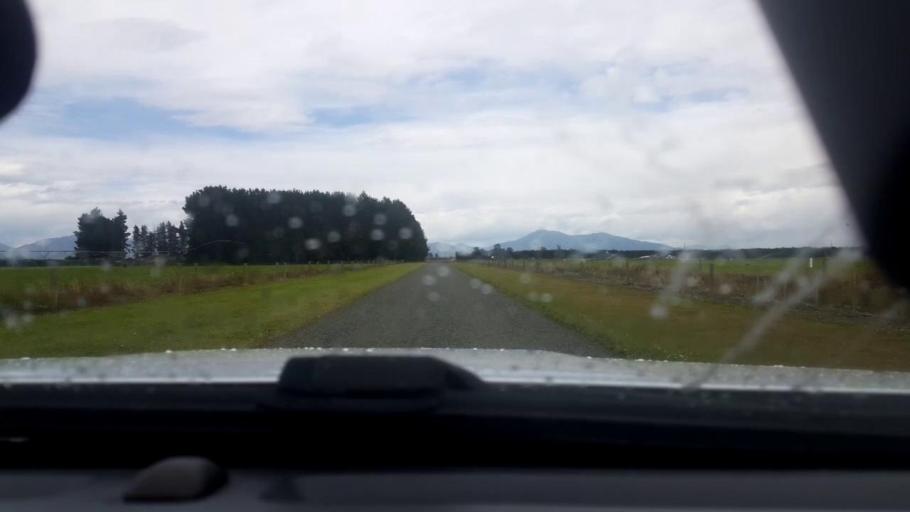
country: NZ
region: Canterbury
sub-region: Timaru District
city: Pleasant Point
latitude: -44.1111
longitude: 171.3515
